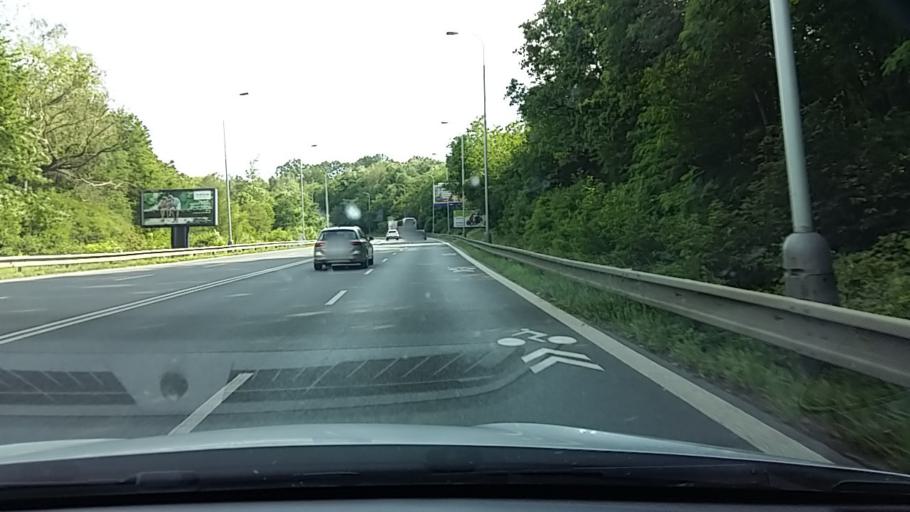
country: CZ
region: Central Bohemia
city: Horomerice
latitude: 50.0634
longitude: 14.3344
